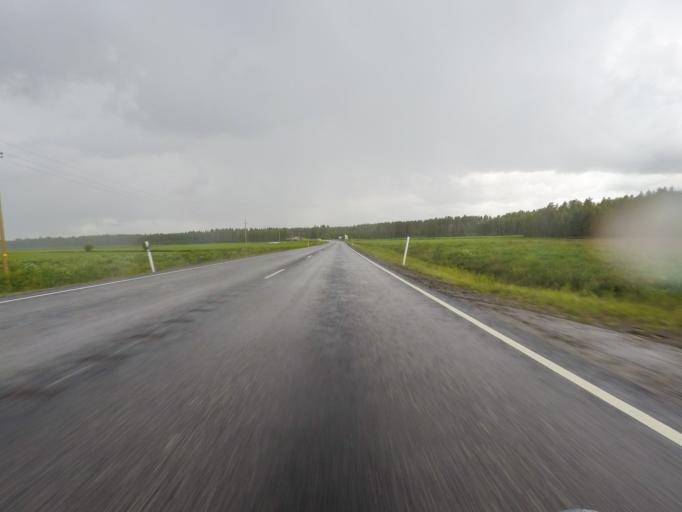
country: FI
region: Central Finland
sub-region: Jyvaeskylae
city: Hankasalmi
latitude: 62.3808
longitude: 26.5968
